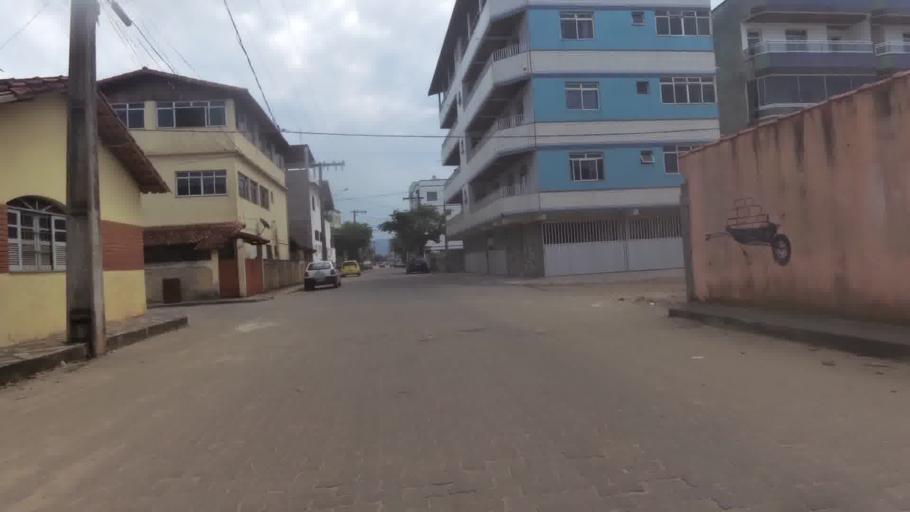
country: BR
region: Espirito Santo
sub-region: Piuma
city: Piuma
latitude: -20.8518
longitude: -40.7492
